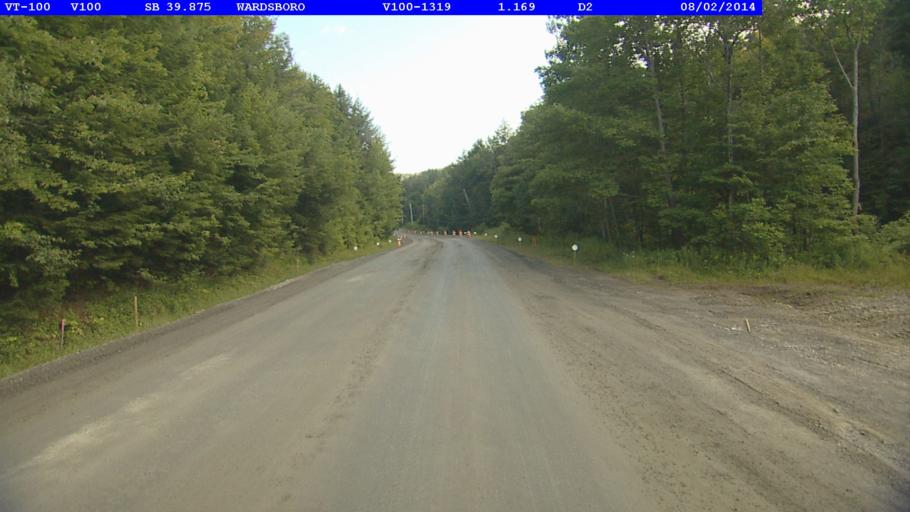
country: US
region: Vermont
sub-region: Windham County
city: Dover
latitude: 43.0164
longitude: -72.8606
